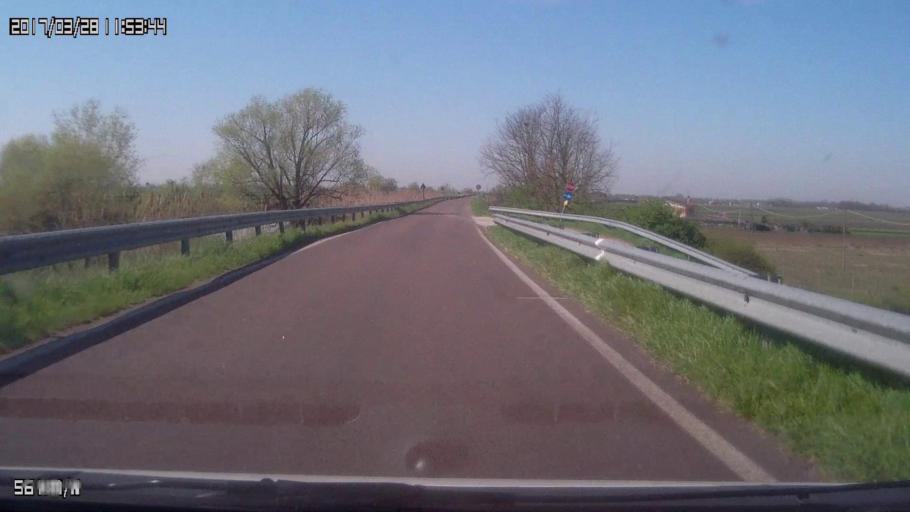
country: IT
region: Veneto
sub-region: Provincia di Venezia
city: Boscochiaro
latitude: 45.1389
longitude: 12.1683
